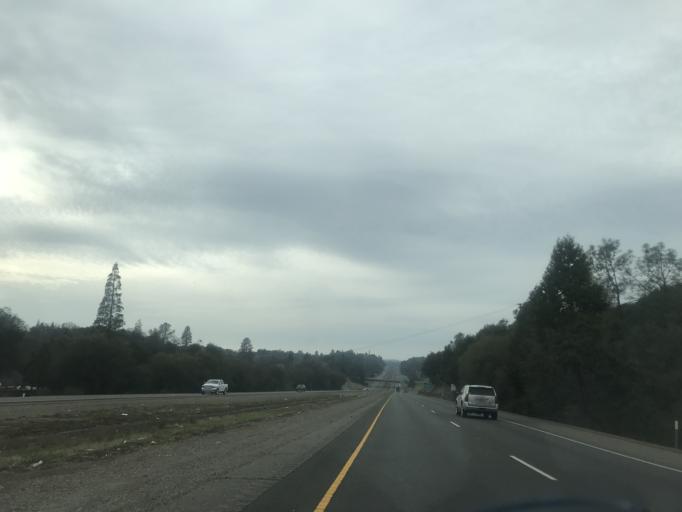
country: US
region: California
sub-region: El Dorado County
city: Deer Park
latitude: 38.7074
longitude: -120.8494
